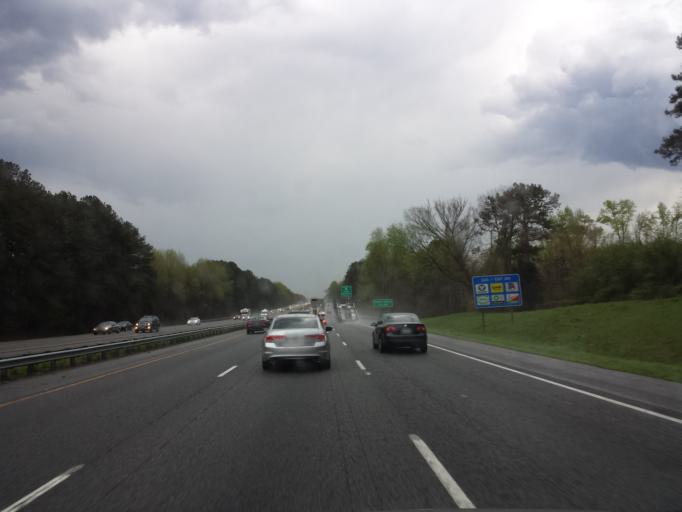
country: US
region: Georgia
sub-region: Henry County
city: Locust Grove
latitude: 33.2243
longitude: -84.0743
